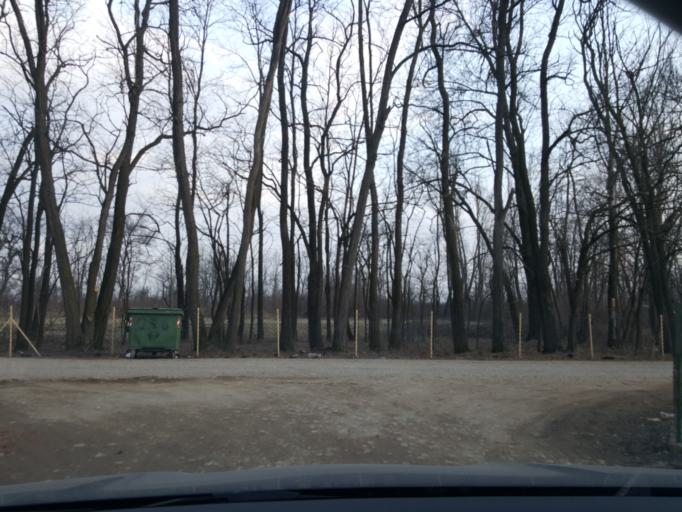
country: RS
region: Central Serbia
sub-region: Nisavski Okrug
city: Aleksinac
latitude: 43.5912
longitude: 21.6179
